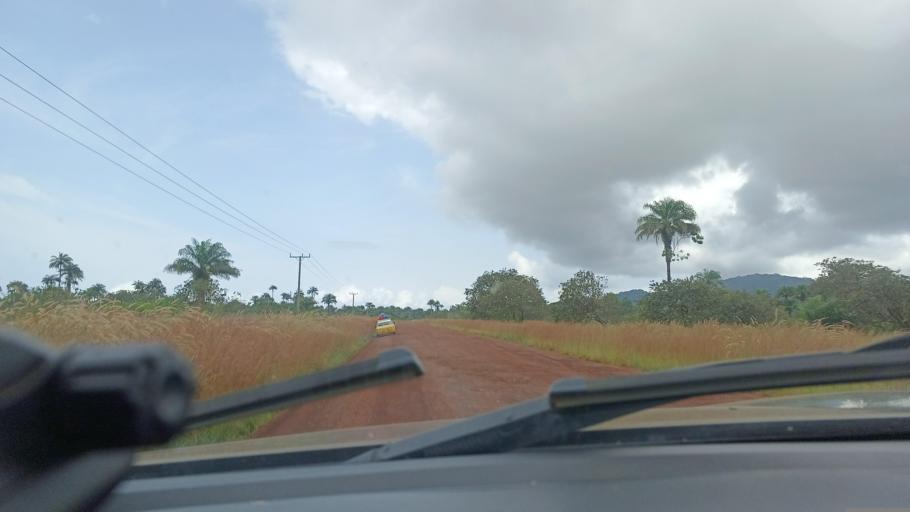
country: LR
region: Grand Cape Mount
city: Robertsport
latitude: 6.7032
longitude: -11.3157
